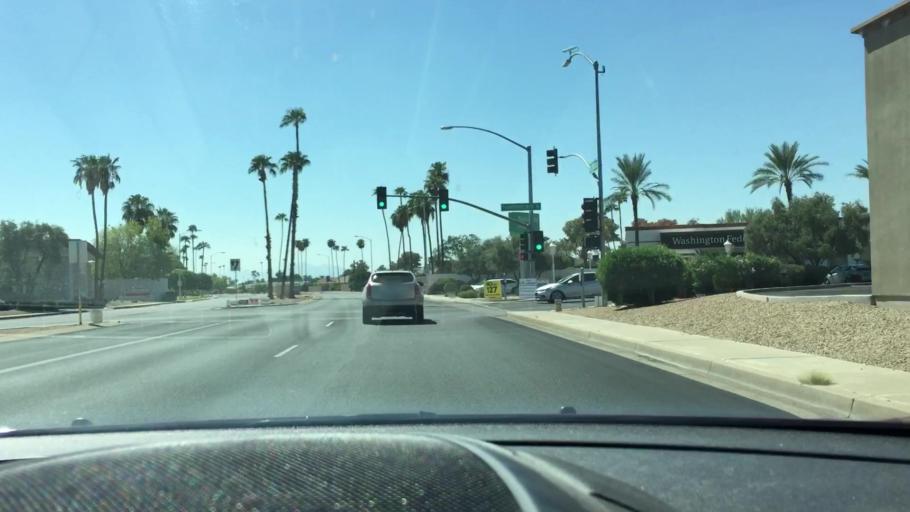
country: US
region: Arizona
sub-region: Maricopa County
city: Youngtown
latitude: 33.6179
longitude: -112.2914
